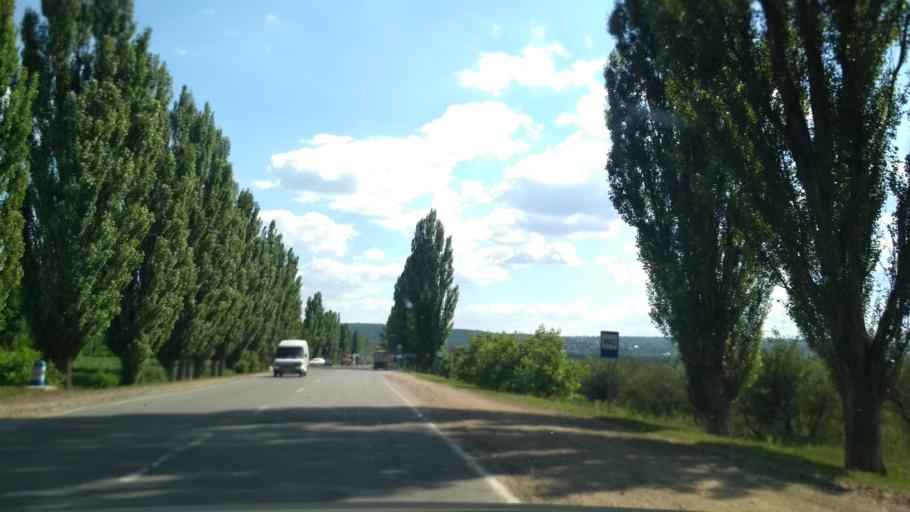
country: MD
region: Chisinau
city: Vadul lui Voda
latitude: 47.1028
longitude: 29.0992
